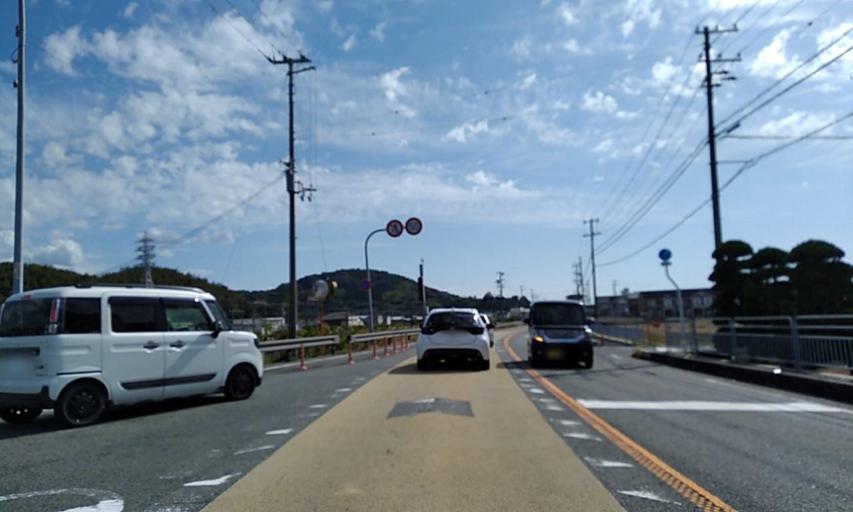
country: JP
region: Wakayama
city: Gobo
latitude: 33.9216
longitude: 135.1457
